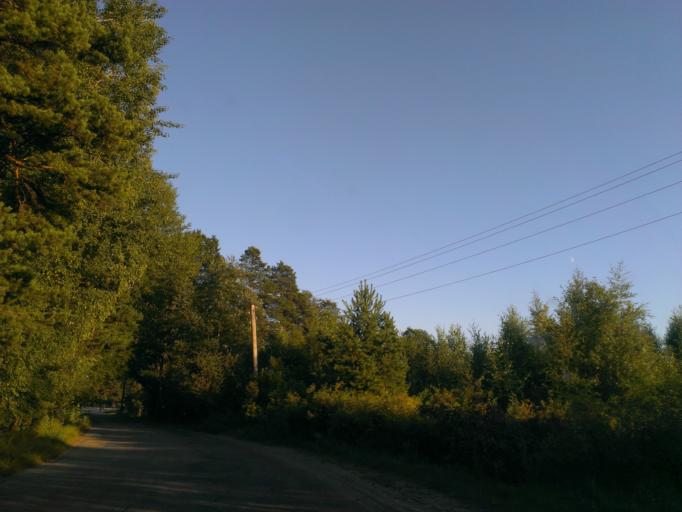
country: LV
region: Garkalne
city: Garkalne
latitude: 57.0488
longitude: 24.4366
